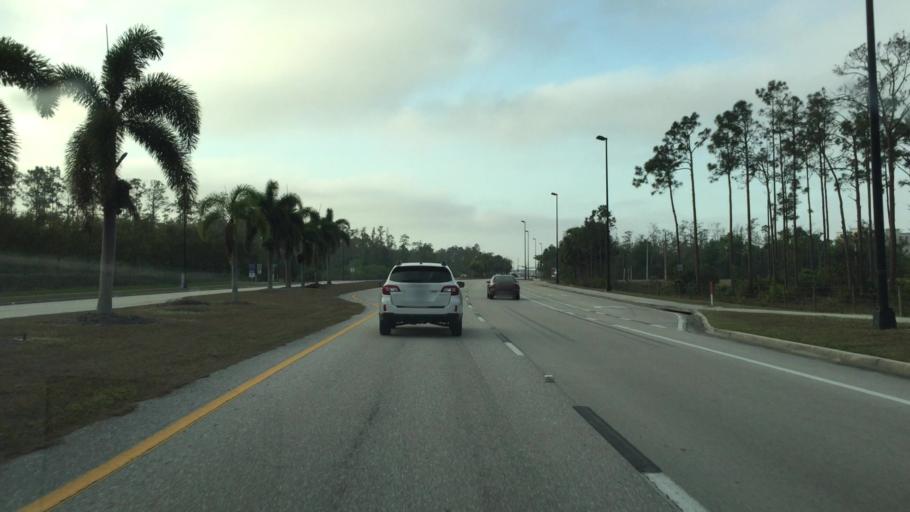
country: US
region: Florida
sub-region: Lee County
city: Three Oaks
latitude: 26.4988
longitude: -81.7841
